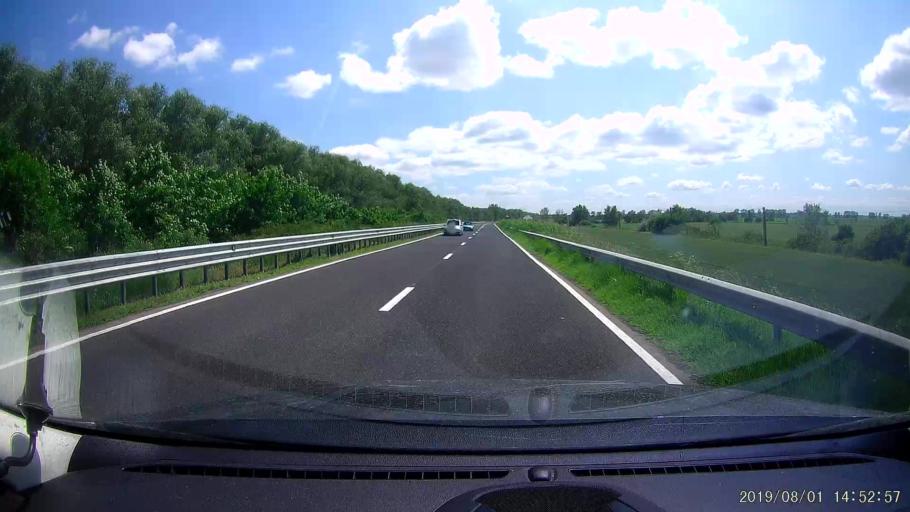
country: RO
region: Braila
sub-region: Comuna Vadeni
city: Vadeni
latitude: 45.3460
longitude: 28.0079
